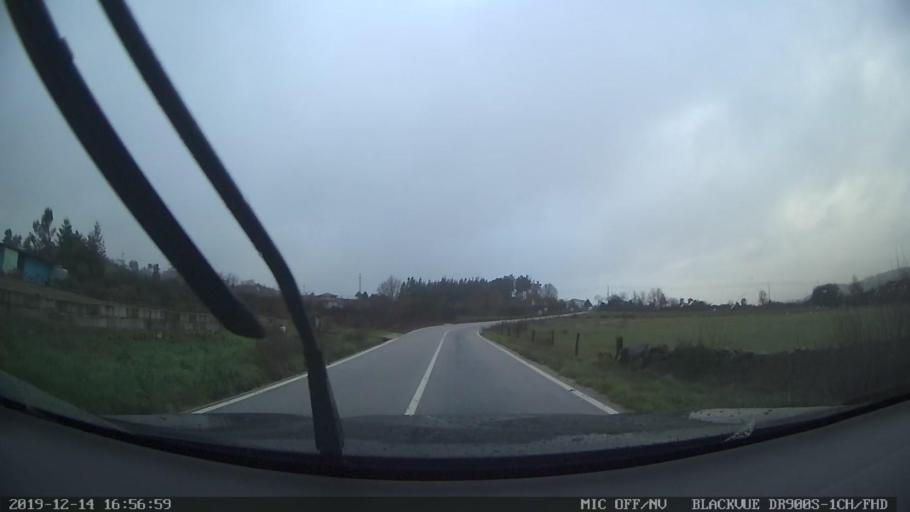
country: PT
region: Vila Real
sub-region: Murca
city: Murca
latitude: 41.4339
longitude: -7.5439
